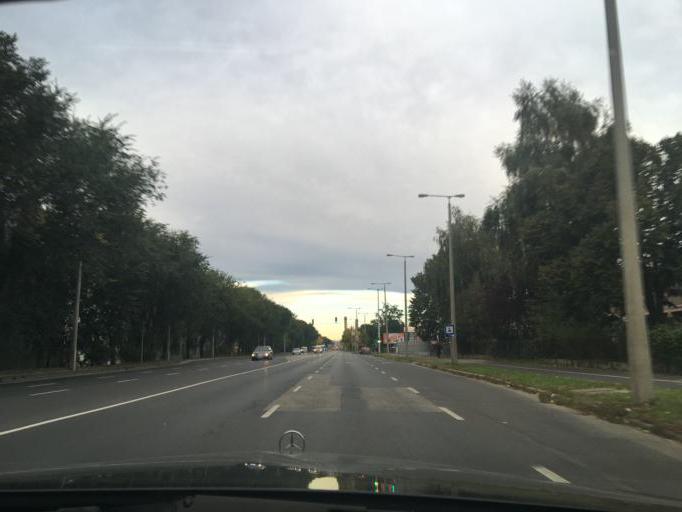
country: HU
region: Hajdu-Bihar
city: Debrecen
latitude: 47.5053
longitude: 21.6306
